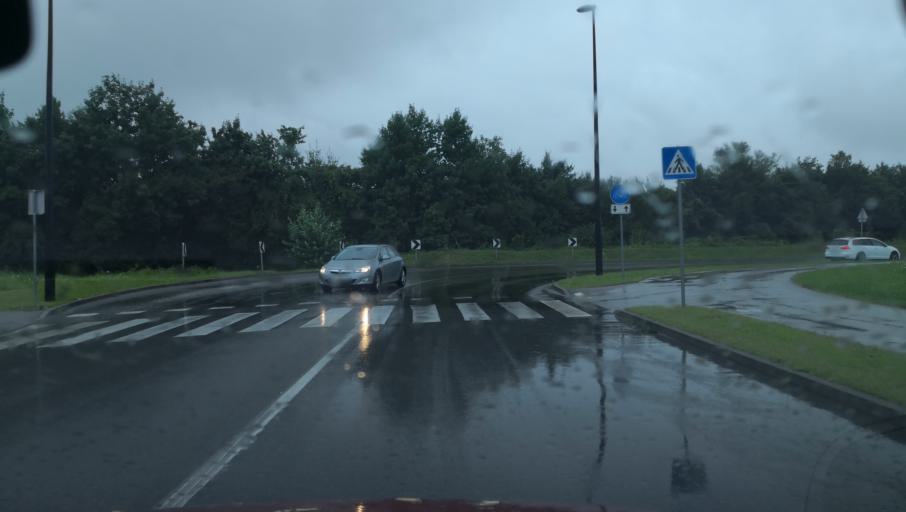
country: SI
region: Ljubljana
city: Ljubljana
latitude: 46.0835
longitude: 14.4981
